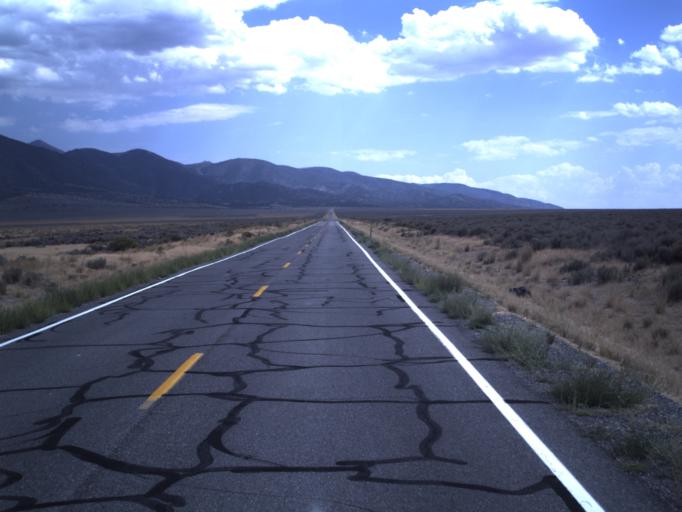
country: US
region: Utah
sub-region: Tooele County
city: Tooele
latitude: 40.3765
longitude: -112.3740
